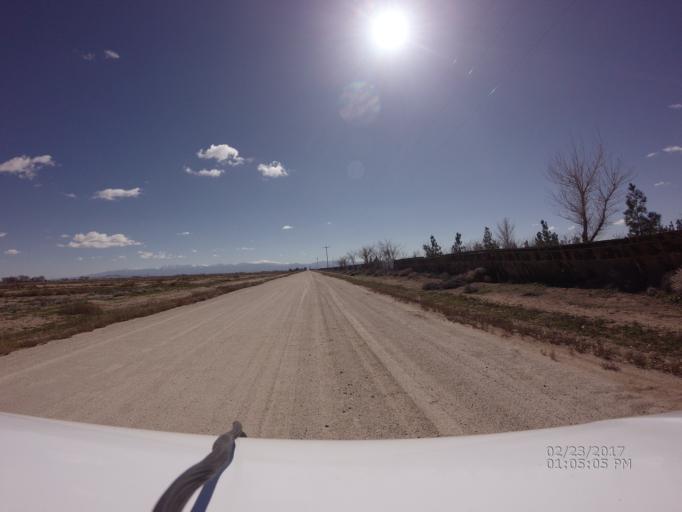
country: US
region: California
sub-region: Los Angeles County
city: Lancaster
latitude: 34.7618
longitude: -118.0145
